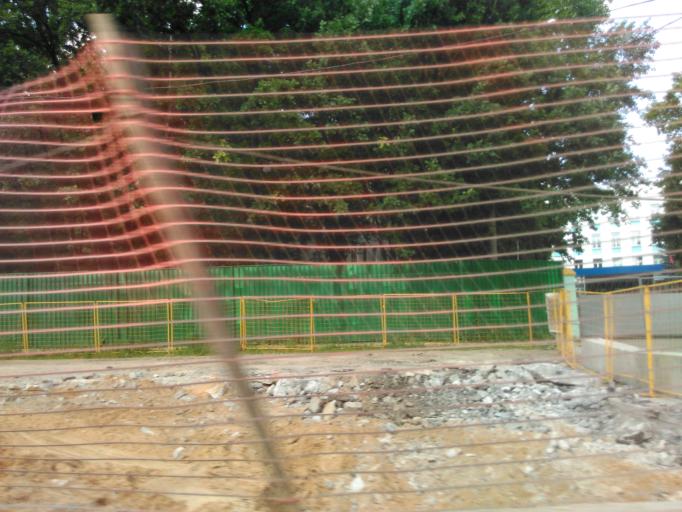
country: RU
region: Moscow
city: Kotlovka
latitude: 55.6641
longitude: 37.6084
